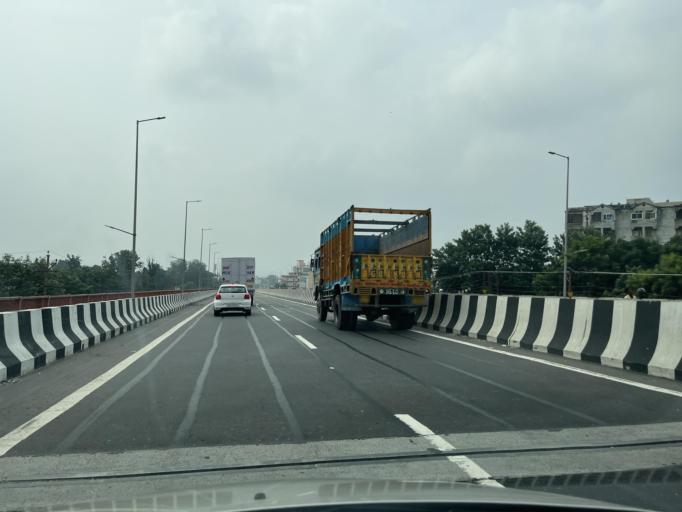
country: IN
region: Uttarakhand
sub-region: Dehradun
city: Raiwala
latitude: 30.0024
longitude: 78.1903
